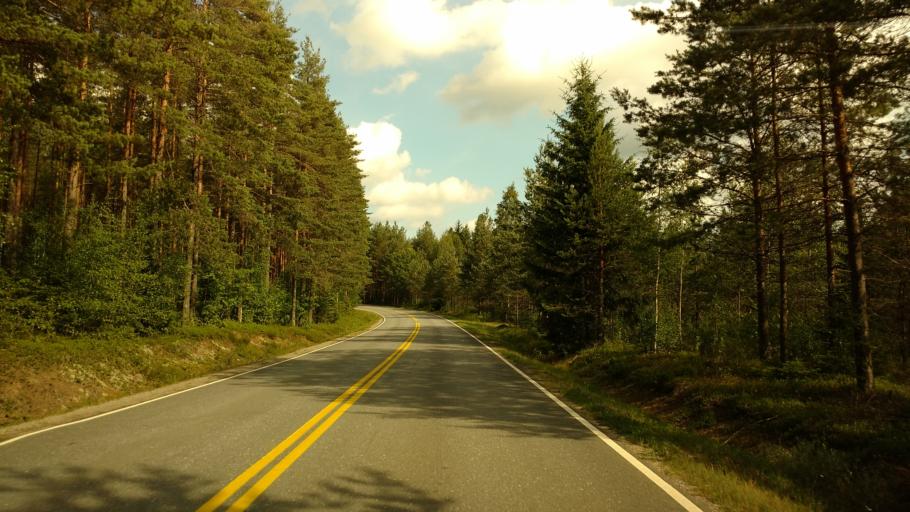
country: FI
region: Varsinais-Suomi
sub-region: Loimaa
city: Koski Tl
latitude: 60.6247
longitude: 23.1121
